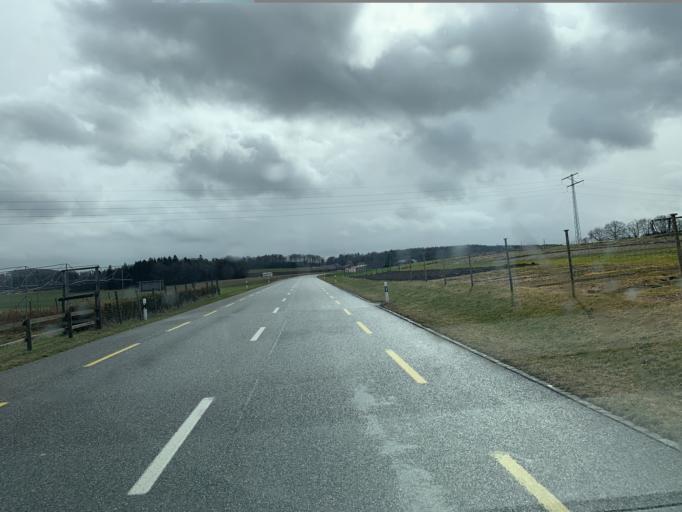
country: CH
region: Fribourg
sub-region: Sense District
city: Dudingen
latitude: 46.8705
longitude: 7.1941
